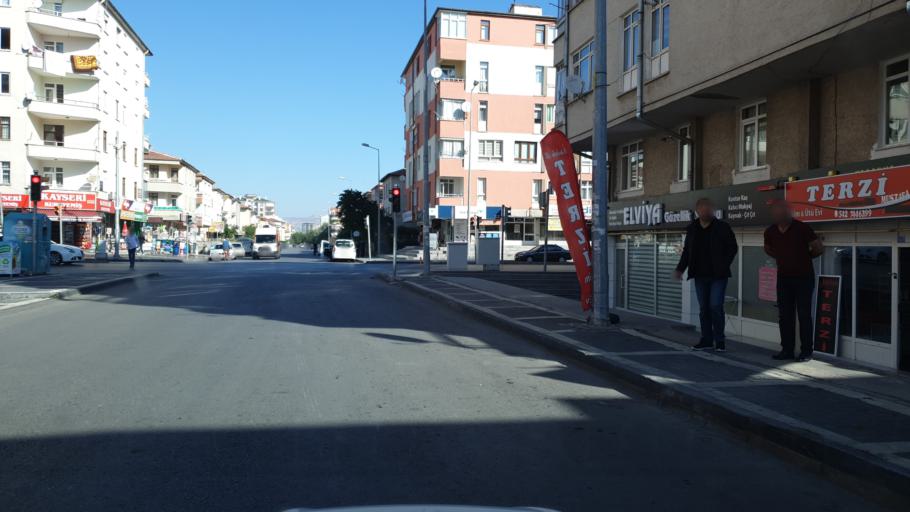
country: TR
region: Kayseri
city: Kayseri
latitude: 38.7381
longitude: 35.4883
